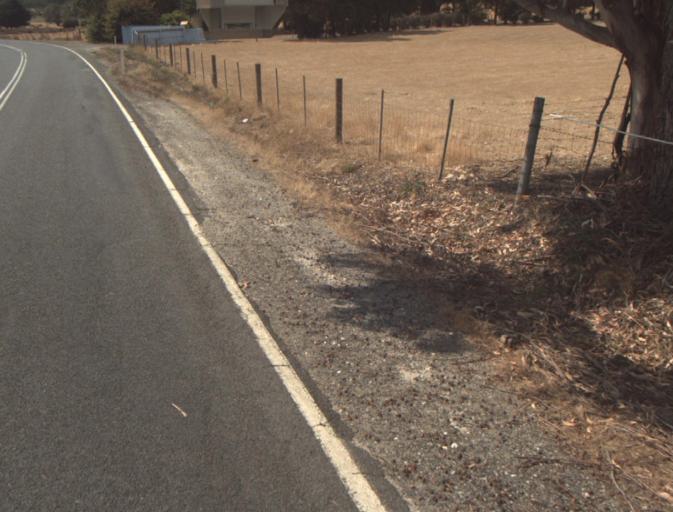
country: AU
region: Tasmania
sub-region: Launceston
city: Newstead
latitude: -41.4415
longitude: 147.2127
